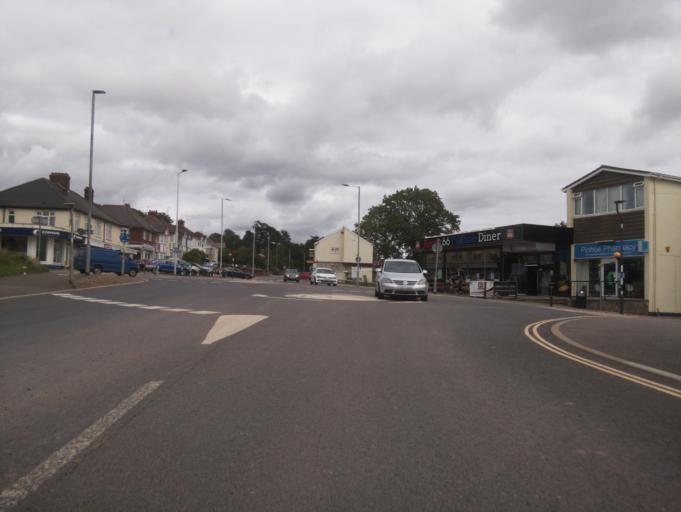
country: GB
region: England
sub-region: Devon
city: Heavitree
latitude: 50.7402
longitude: -3.4698
